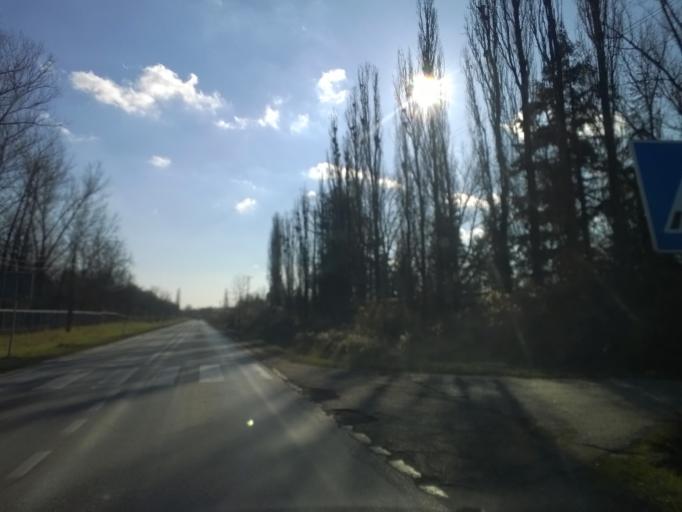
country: RS
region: Central Serbia
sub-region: Podunavski Okrug
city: Smederevo
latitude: 44.6029
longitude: 20.9626
